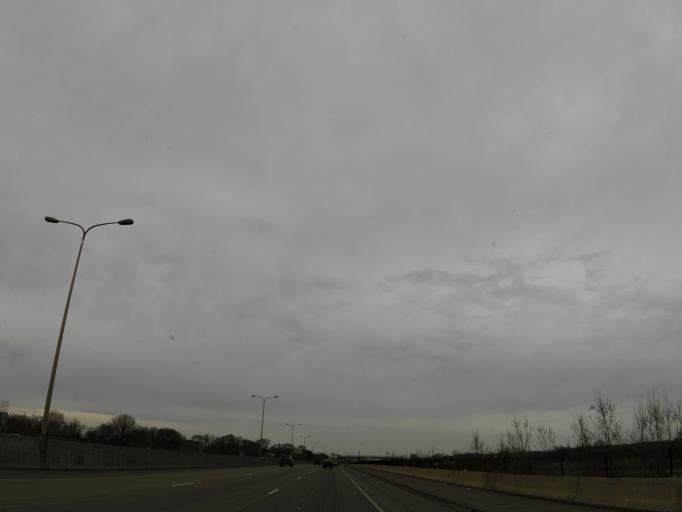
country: US
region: Minnesota
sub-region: Washington County
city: Newport
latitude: 44.8593
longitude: -92.9959
